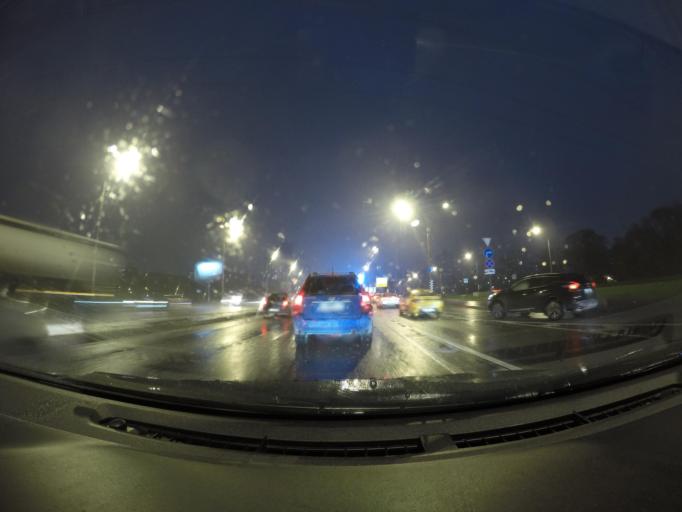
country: RU
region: Moskovskaya
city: Kozhukhovo
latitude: 55.6990
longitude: 37.6663
